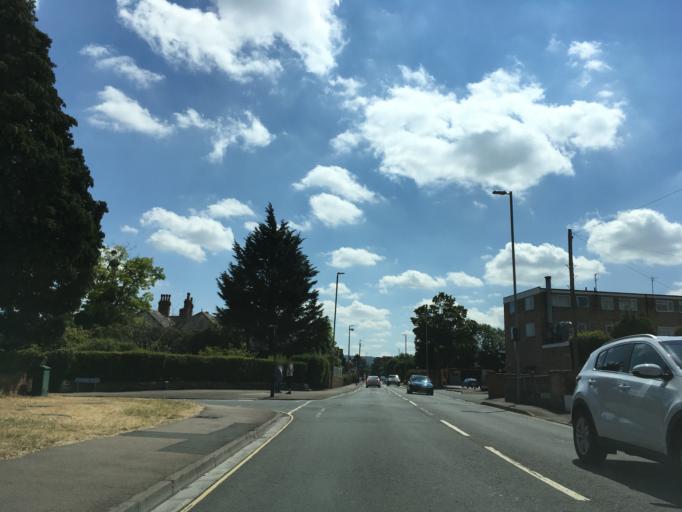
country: GB
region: England
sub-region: Gloucestershire
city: Barnwood
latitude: 51.8560
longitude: -2.1893
